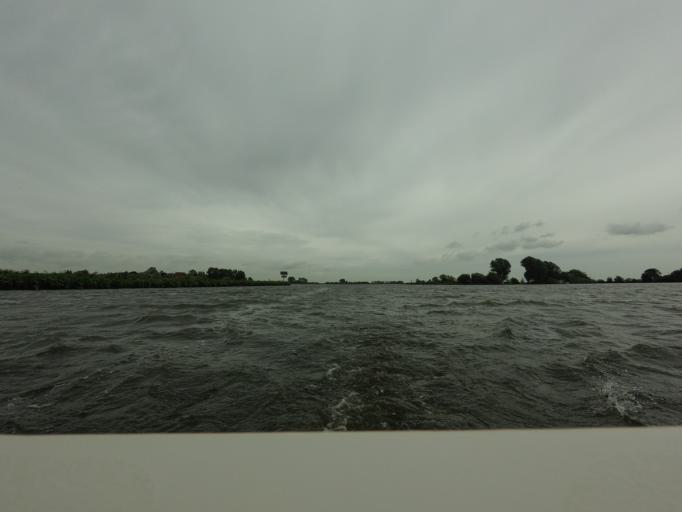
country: NL
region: Friesland
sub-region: Gemeente Boarnsterhim
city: Grou
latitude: 53.1053
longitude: 5.8549
